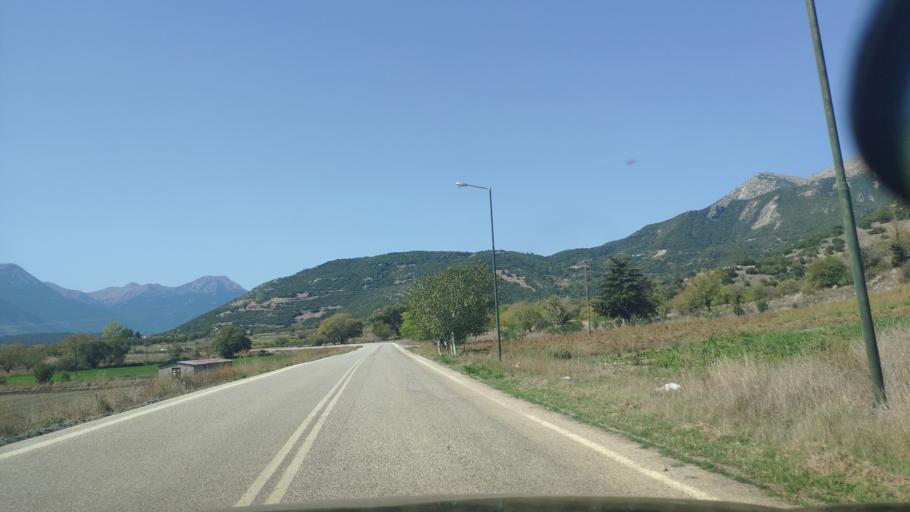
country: GR
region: Peloponnese
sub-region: Nomos Korinthias
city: Nemea
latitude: 37.8785
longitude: 22.4804
